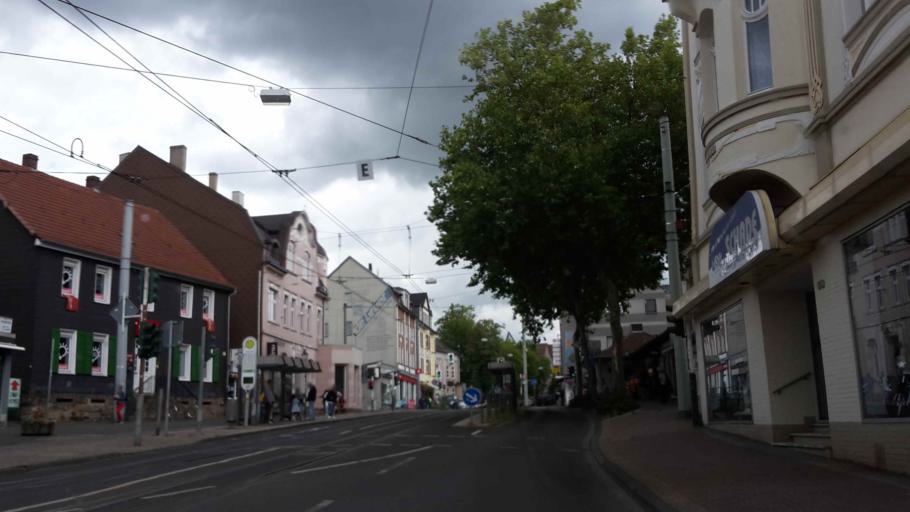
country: DE
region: North Rhine-Westphalia
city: Hattingen
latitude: 51.4255
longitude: 7.1604
